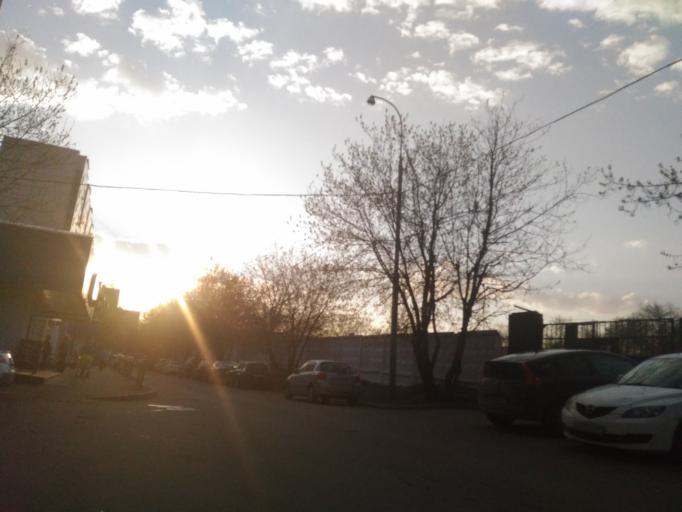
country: RU
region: Moskovskaya
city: Khoroshevo-Mnevniki
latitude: 55.7880
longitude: 37.4739
